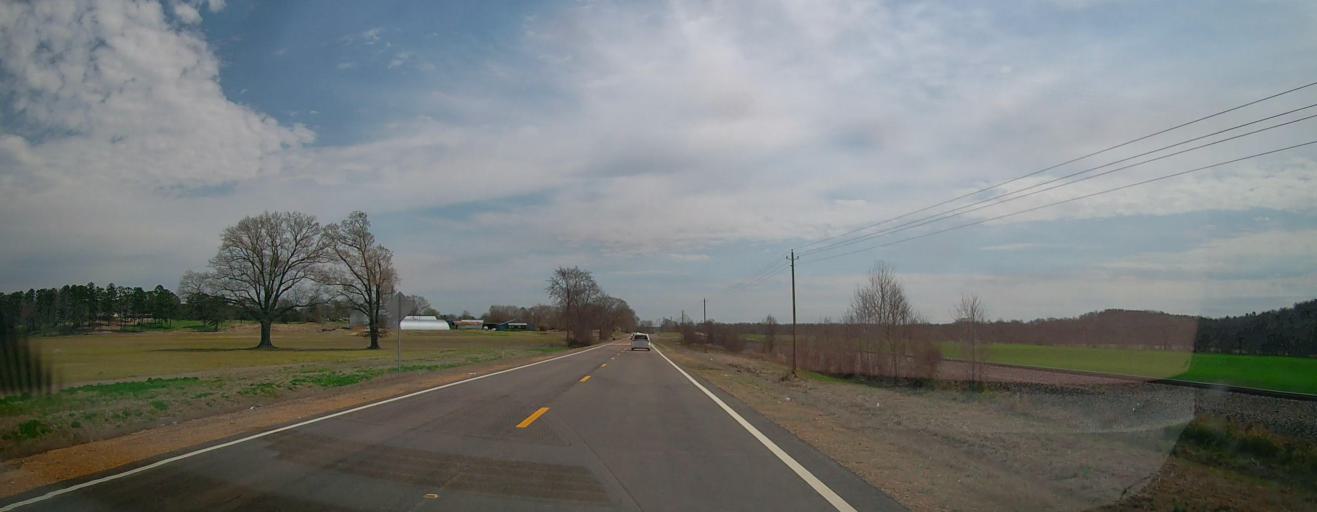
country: US
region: Mississippi
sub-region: Benton County
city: Ashland
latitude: 34.6220
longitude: -89.2366
